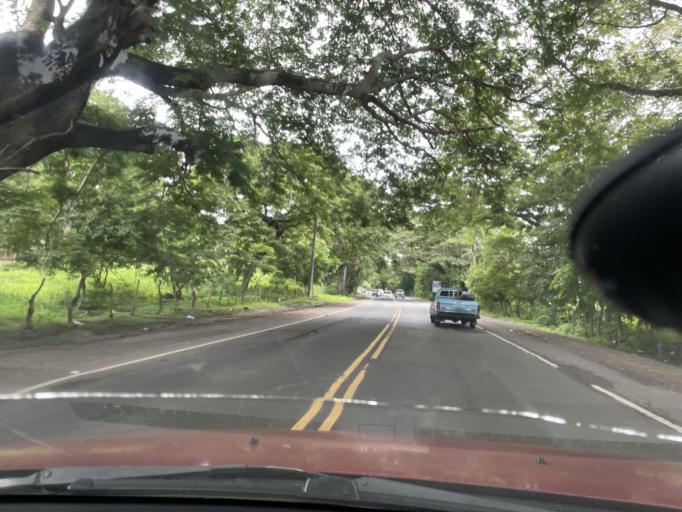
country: SV
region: Usulutan
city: Jucuaran
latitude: 13.3317
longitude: -88.1765
